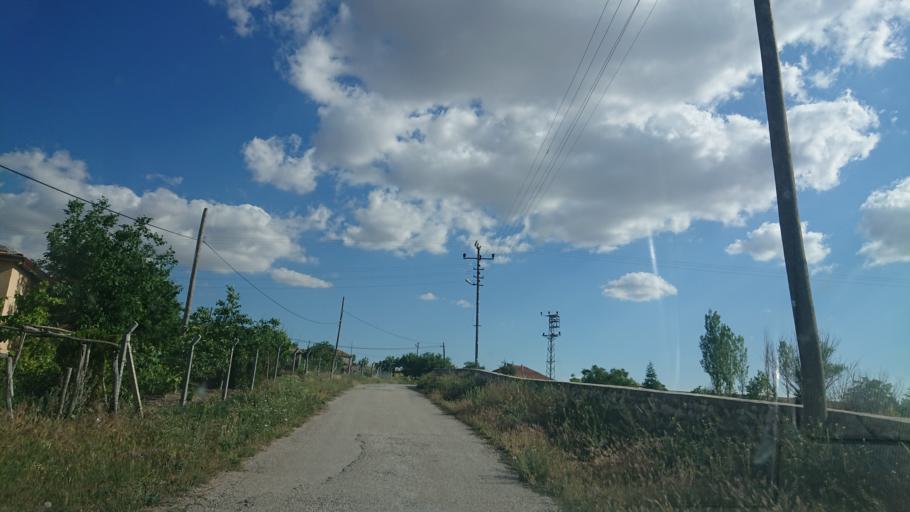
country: TR
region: Aksaray
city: Agacoren
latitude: 38.7533
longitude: 33.8850
